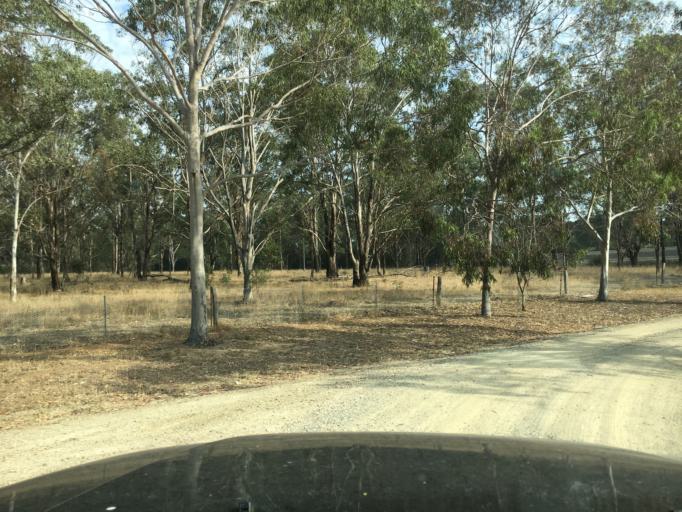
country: AU
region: New South Wales
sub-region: Cessnock
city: Branxton
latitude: -32.6665
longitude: 151.3035
